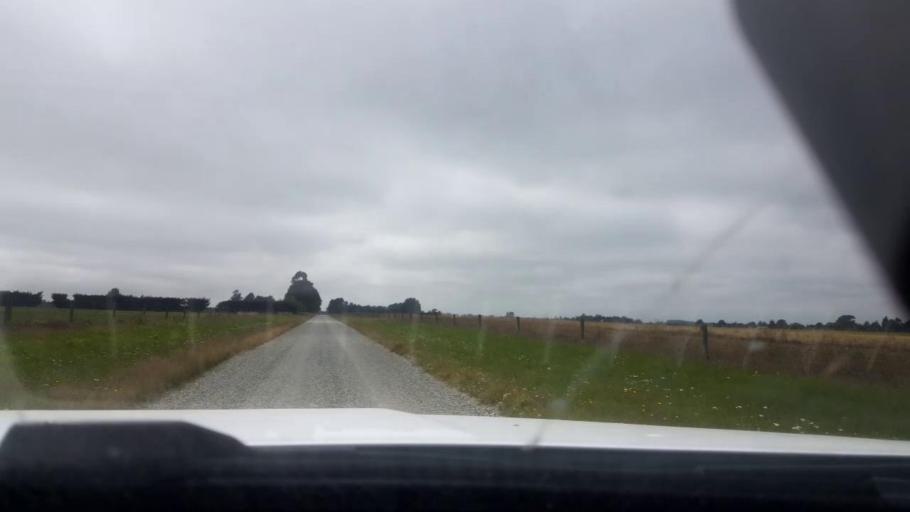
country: NZ
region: Canterbury
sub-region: Timaru District
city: Pleasant Point
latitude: -44.2872
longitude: 171.2018
